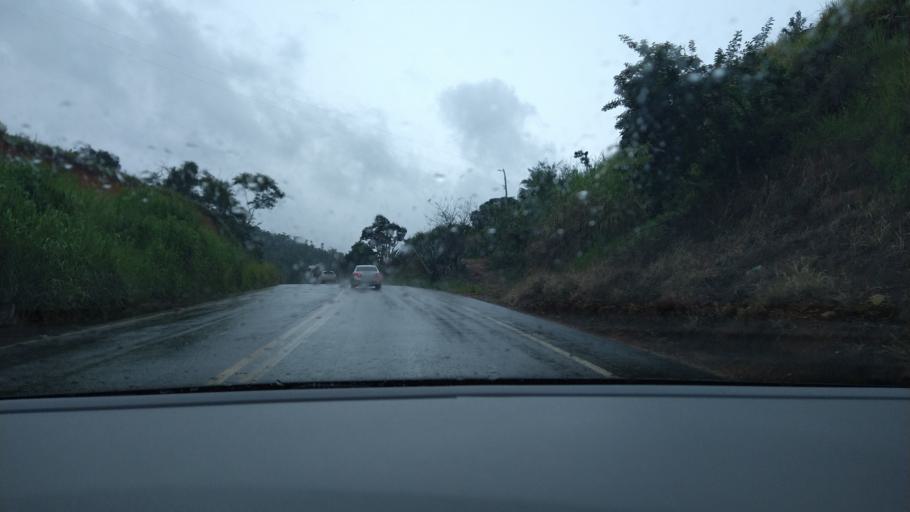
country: BR
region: Minas Gerais
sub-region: Vicosa
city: Vicosa
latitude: -20.6171
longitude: -42.8674
